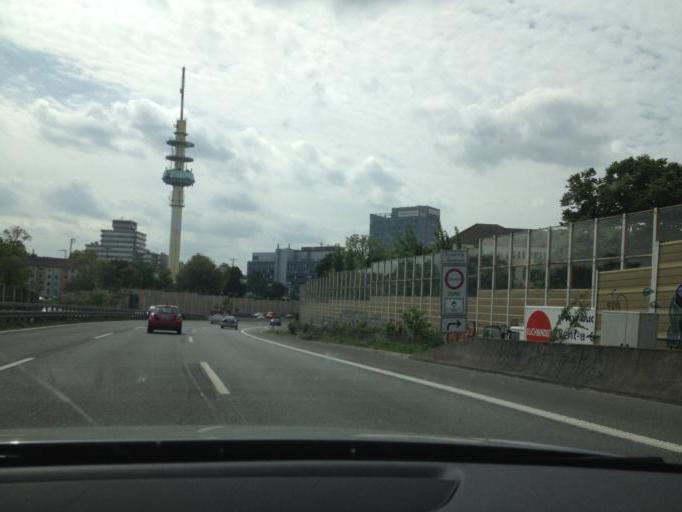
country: DE
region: North Rhine-Westphalia
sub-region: Regierungsbezirk Dusseldorf
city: Duisburg
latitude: 51.4366
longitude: 6.7757
